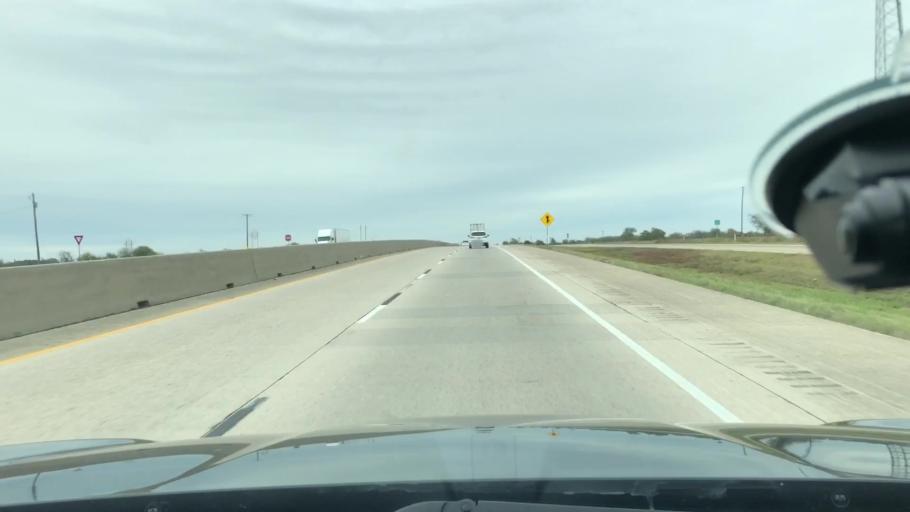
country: US
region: Texas
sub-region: Hunt County
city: Commerce
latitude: 33.1314
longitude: -95.8016
